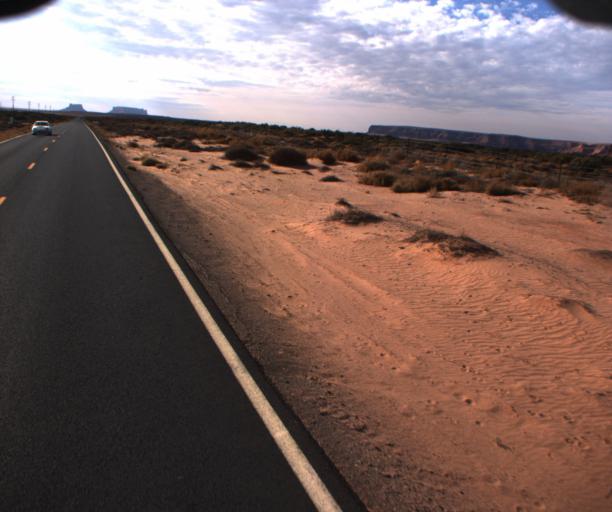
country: US
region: Arizona
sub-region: Apache County
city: Many Farms
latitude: 36.6504
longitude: -109.5920
